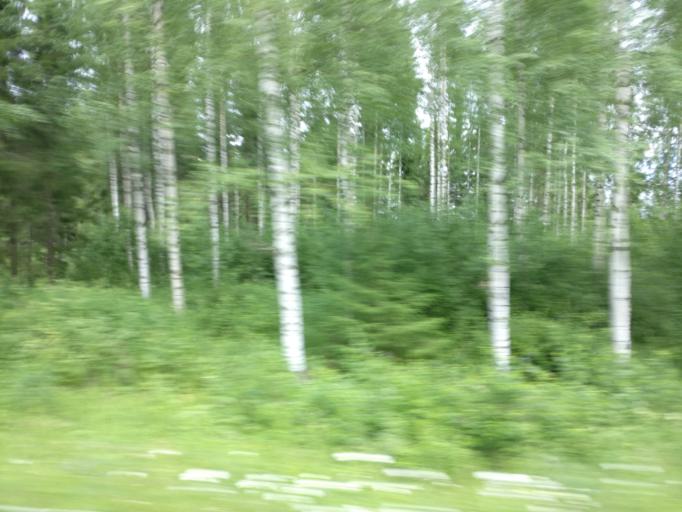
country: FI
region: Northern Savo
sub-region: Koillis-Savo
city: Juankoski
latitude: 62.9935
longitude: 28.2543
